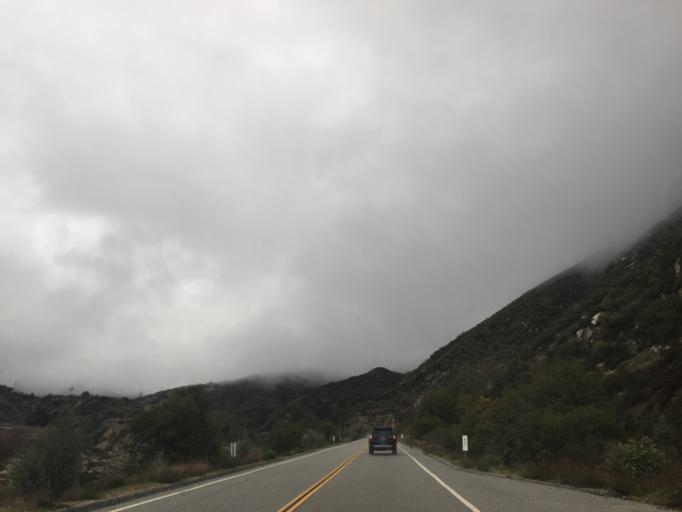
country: US
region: California
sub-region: Los Angeles County
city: Glendora
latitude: 34.2802
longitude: -117.8395
